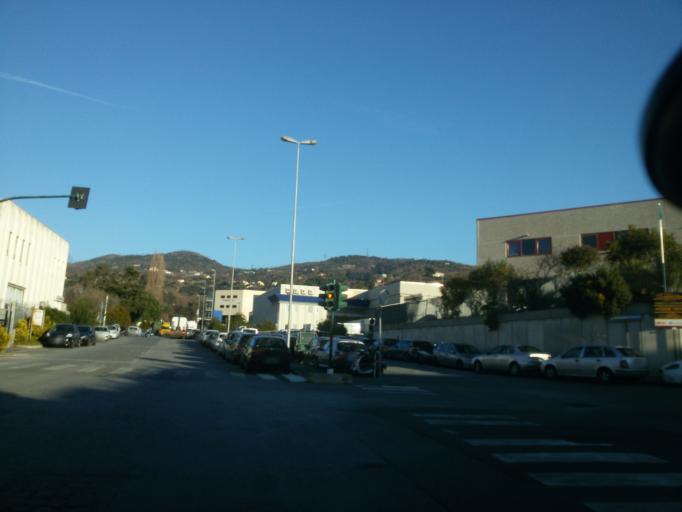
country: IT
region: Liguria
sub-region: Provincia di Savona
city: Savona
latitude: 44.3009
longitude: 8.4553
